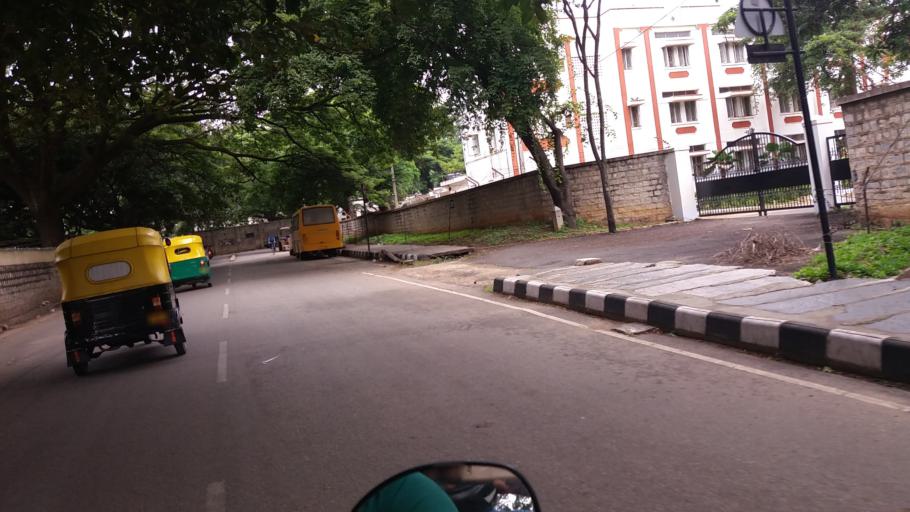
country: IN
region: Karnataka
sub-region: Bangalore Urban
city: Bangalore
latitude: 12.9716
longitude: 77.6245
